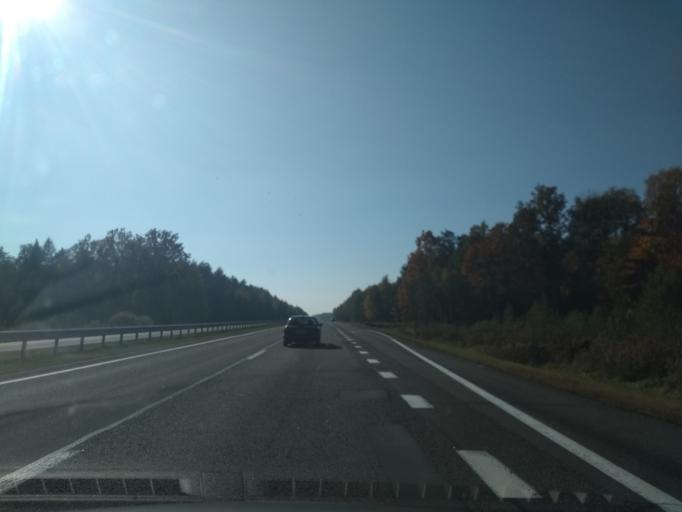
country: BY
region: Brest
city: Ivatsevichy
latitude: 52.8215
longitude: 25.5880
